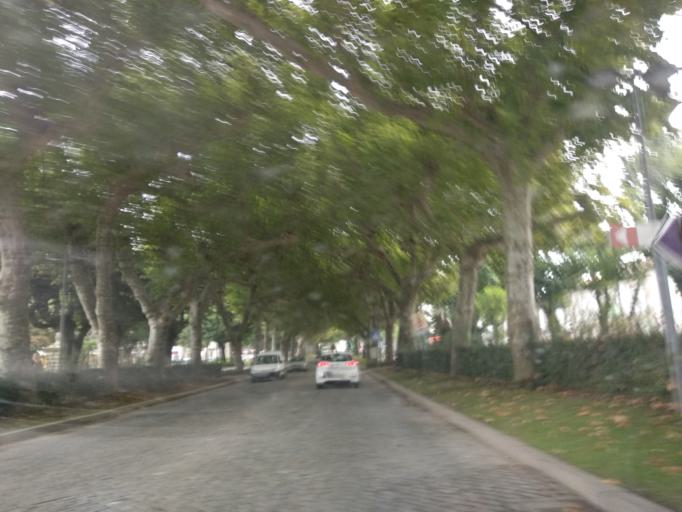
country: PT
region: Braga
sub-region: Vila Verde
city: Vila Verde
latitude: 41.6497
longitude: -8.4356
